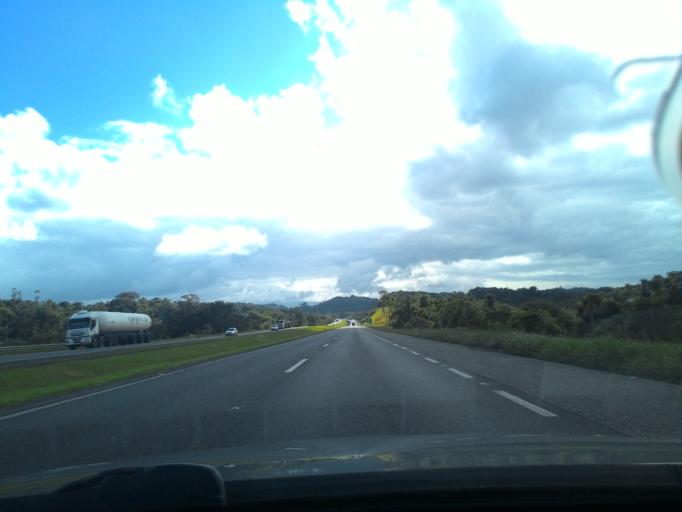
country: BR
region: Sao Paulo
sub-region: Cajati
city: Cajati
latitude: -24.9371
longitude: -48.2957
